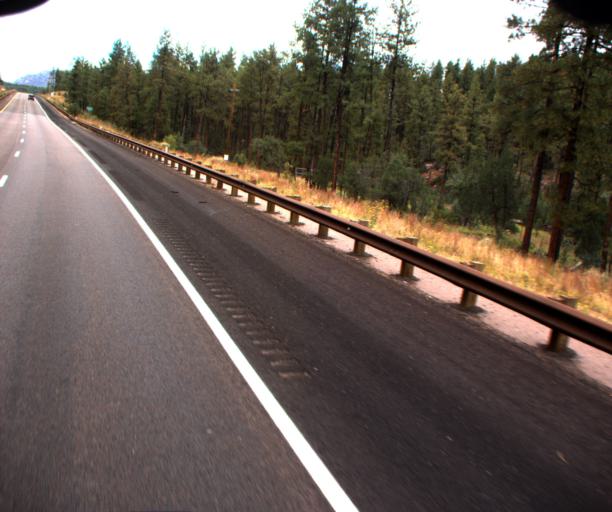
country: US
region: Arizona
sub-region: Gila County
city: Star Valley
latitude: 34.3088
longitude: -111.1090
